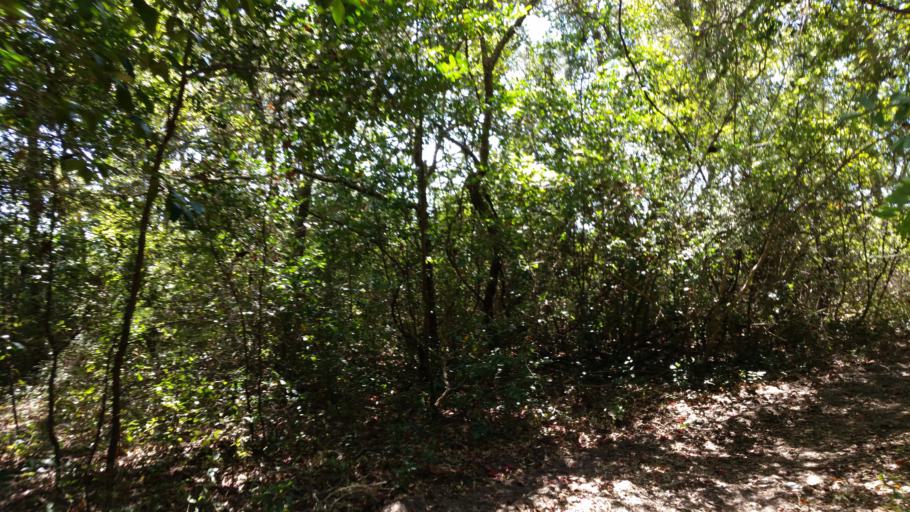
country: US
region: Florida
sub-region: Santa Rosa County
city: Gulf Breeze
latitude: 30.3615
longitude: -87.1397
